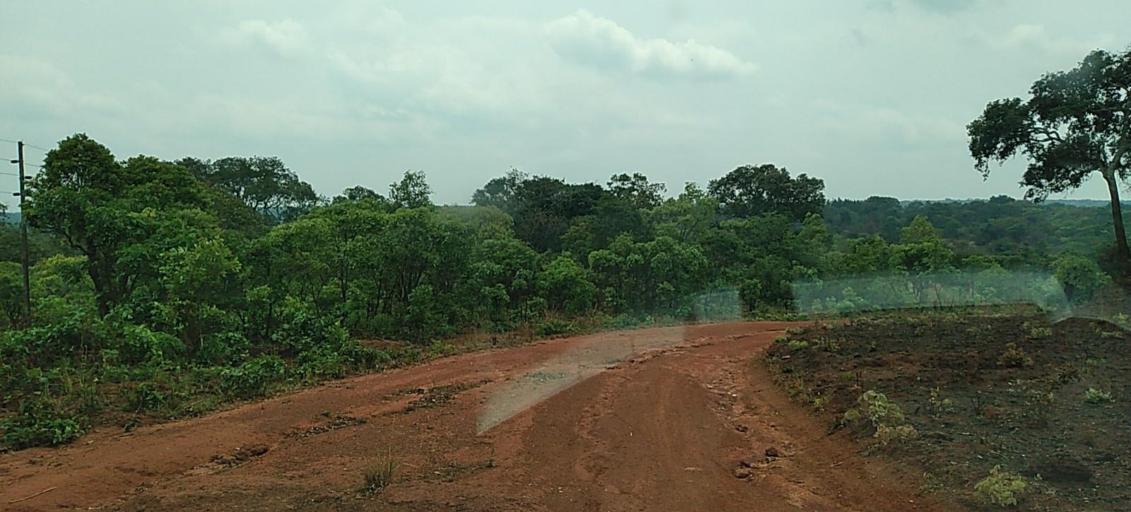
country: ZM
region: North-Western
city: Mwinilunga
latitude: -11.5138
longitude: 24.7887
